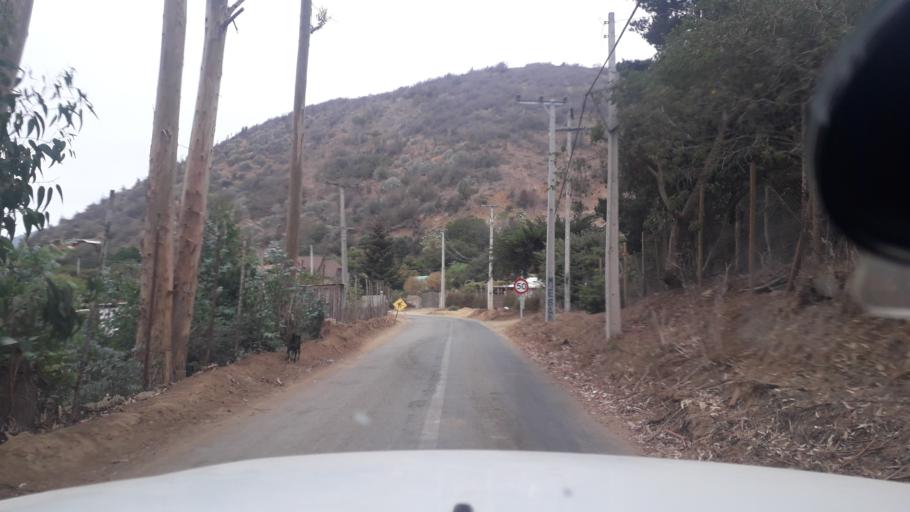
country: CL
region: Valparaiso
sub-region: Provincia de Valparaiso
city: Valparaiso
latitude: -33.1129
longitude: -71.6568
